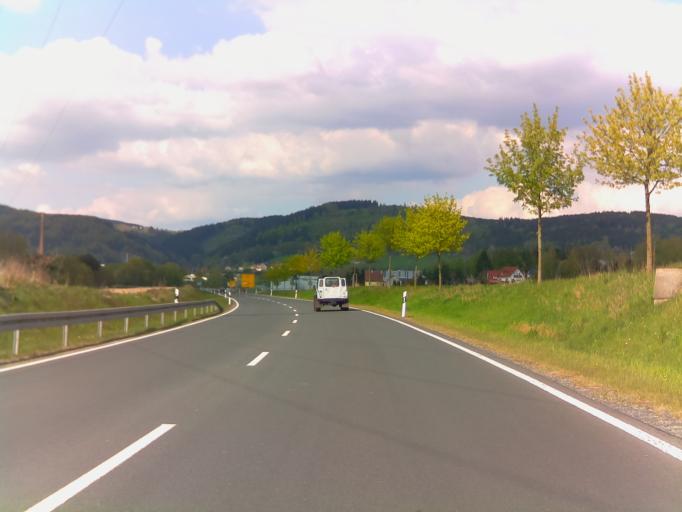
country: DE
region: Bavaria
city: Foritz
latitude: 50.3383
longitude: 11.2040
